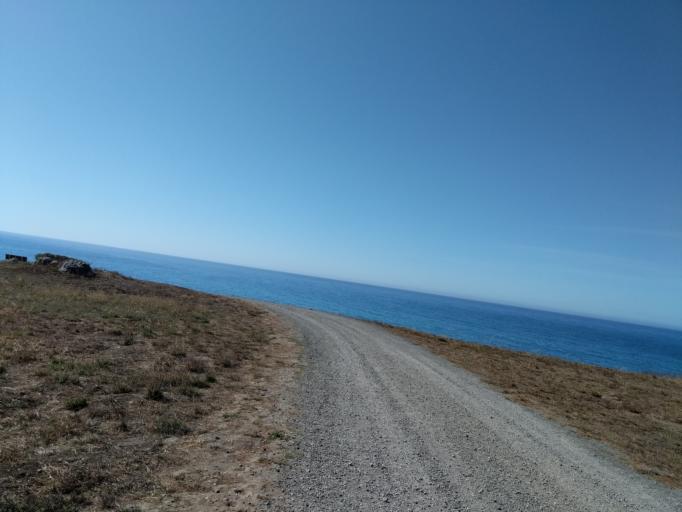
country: US
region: California
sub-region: Sonoma County
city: Monte Rio
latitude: 38.5124
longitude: -123.2445
